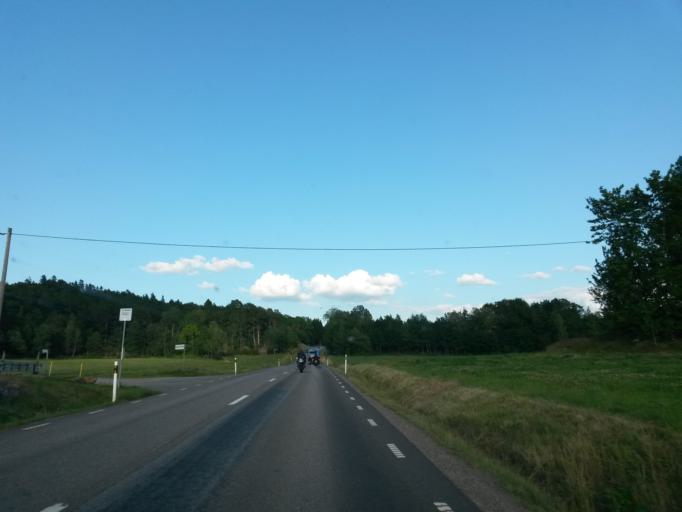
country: SE
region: Vaestra Goetaland
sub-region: Alingsas Kommun
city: Alingsas
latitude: 57.9535
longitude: 12.4691
